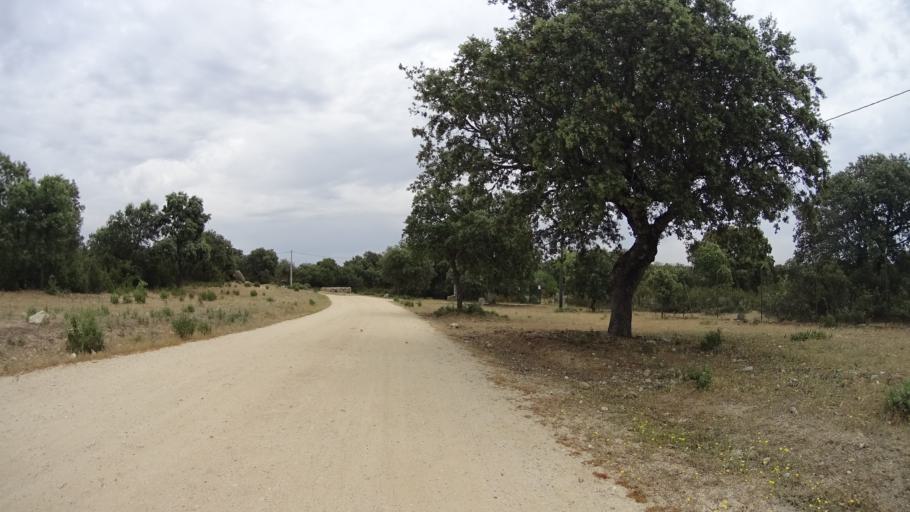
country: ES
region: Madrid
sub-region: Provincia de Madrid
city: Colmenarejo
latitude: 40.5606
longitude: -4.0348
